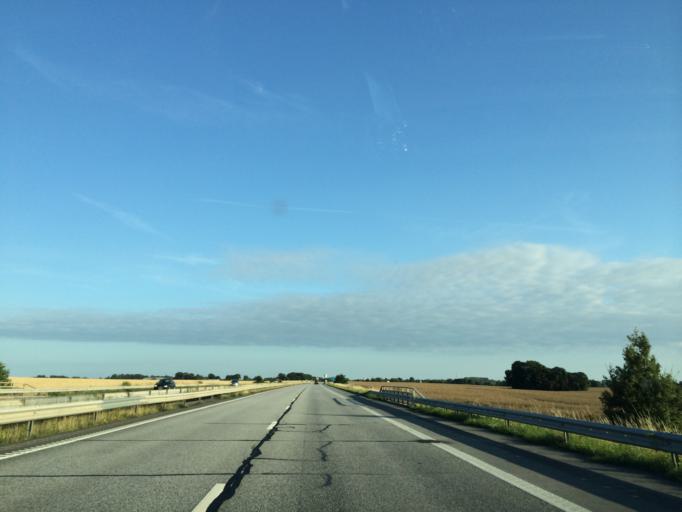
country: SE
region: Skane
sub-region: Malmo
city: Tygelsjo
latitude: 55.4992
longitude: 13.0194
